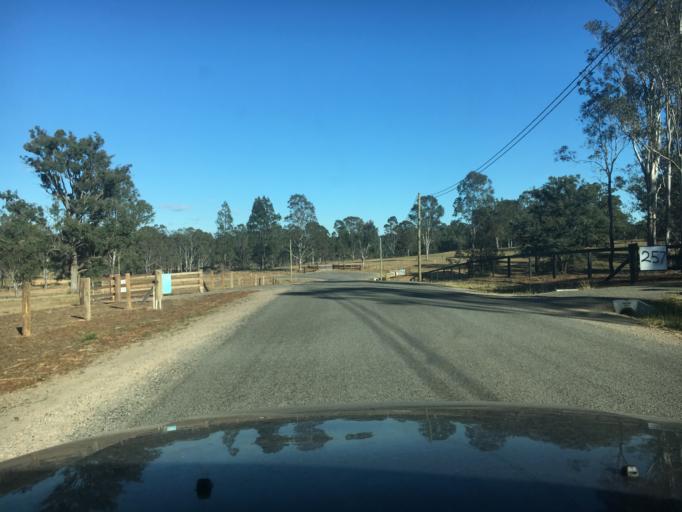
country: AU
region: New South Wales
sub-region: Singleton
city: Singleton
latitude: -32.5338
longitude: 151.2274
